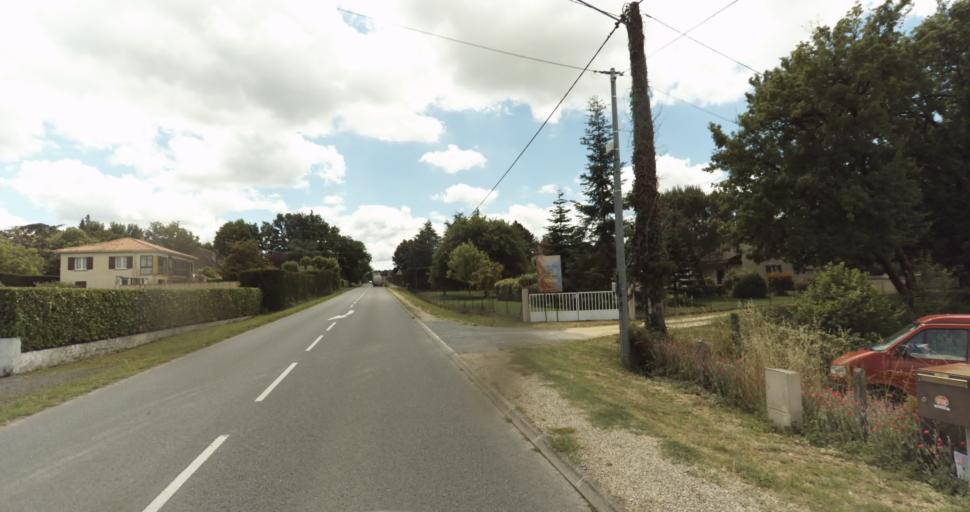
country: FR
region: Aquitaine
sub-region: Departement de la Dordogne
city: Beaumont-du-Perigord
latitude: 44.7570
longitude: 0.7722
